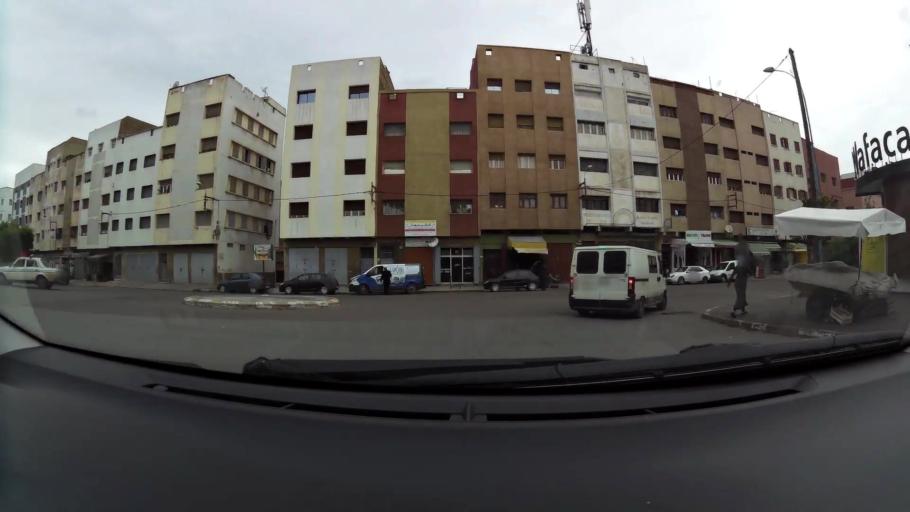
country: MA
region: Grand Casablanca
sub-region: Casablanca
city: Casablanca
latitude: 33.5730
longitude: -7.5599
